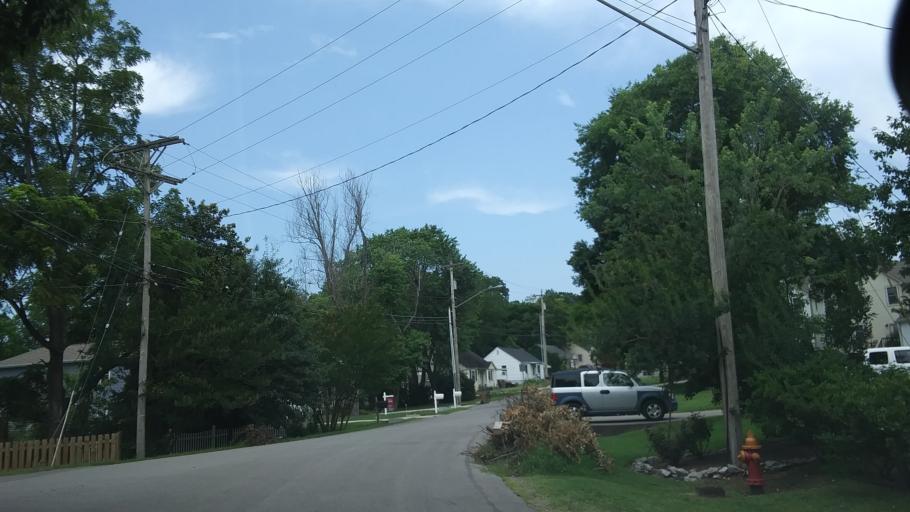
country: US
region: Tennessee
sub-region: Davidson County
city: Belle Meade
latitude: 36.1512
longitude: -86.8730
